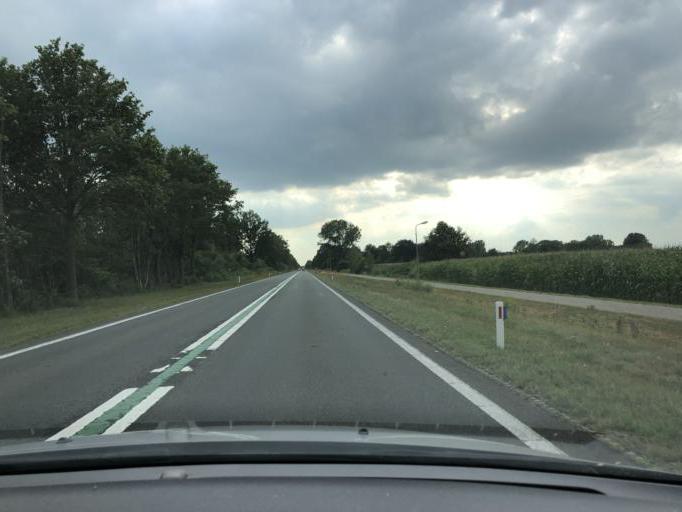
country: NL
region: Overijssel
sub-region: Gemeente Hardenberg
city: Hardenberg
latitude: 52.6140
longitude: 6.5175
